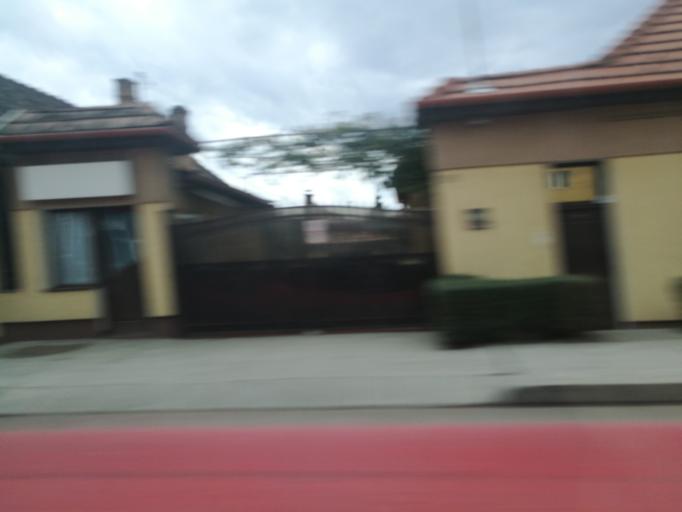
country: RO
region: Mures
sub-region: Comuna Sangeorgiu de Mures
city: Sangeorgiu de Mures
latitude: 46.5717
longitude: 24.5971
